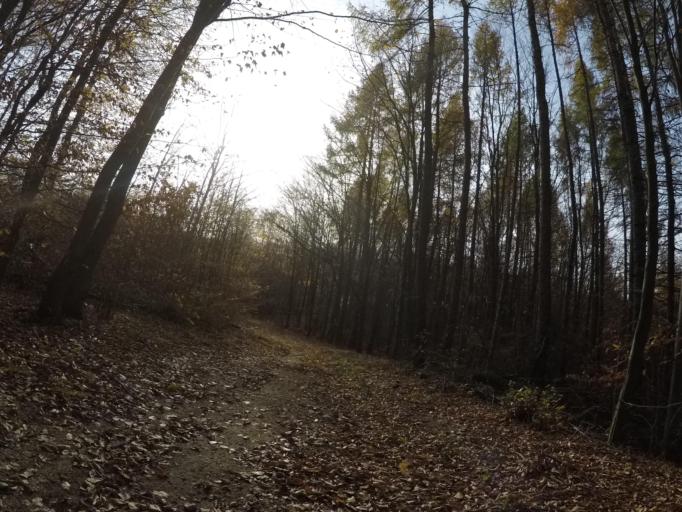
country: SK
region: Presovsky
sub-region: Okres Presov
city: Presov
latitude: 48.9647
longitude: 21.1829
